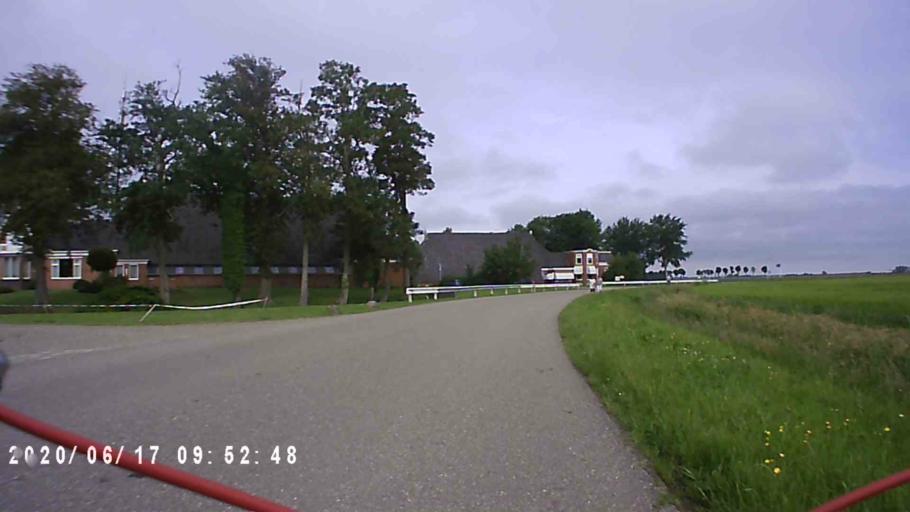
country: NL
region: Groningen
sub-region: Gemeente De Marne
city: Ulrum
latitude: 53.3599
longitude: 6.3206
